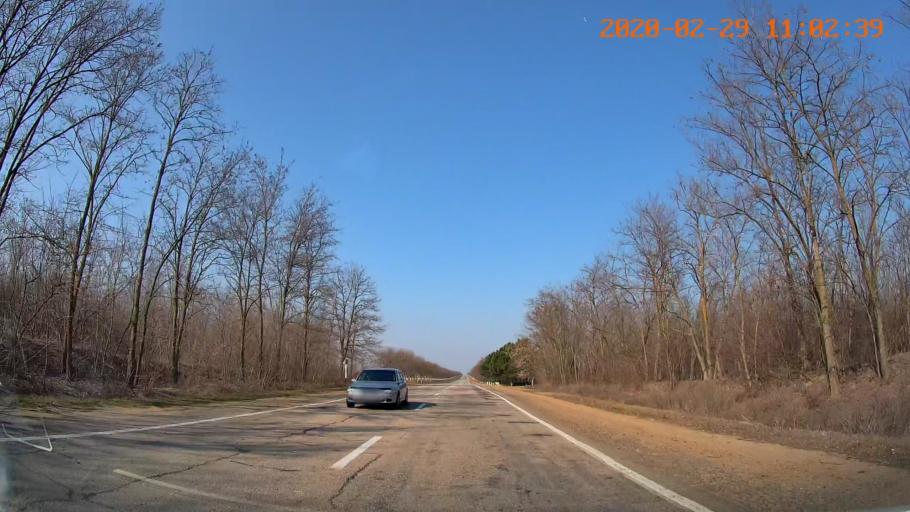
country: MD
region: Telenesti
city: Grigoriopol
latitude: 47.1740
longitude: 29.2338
